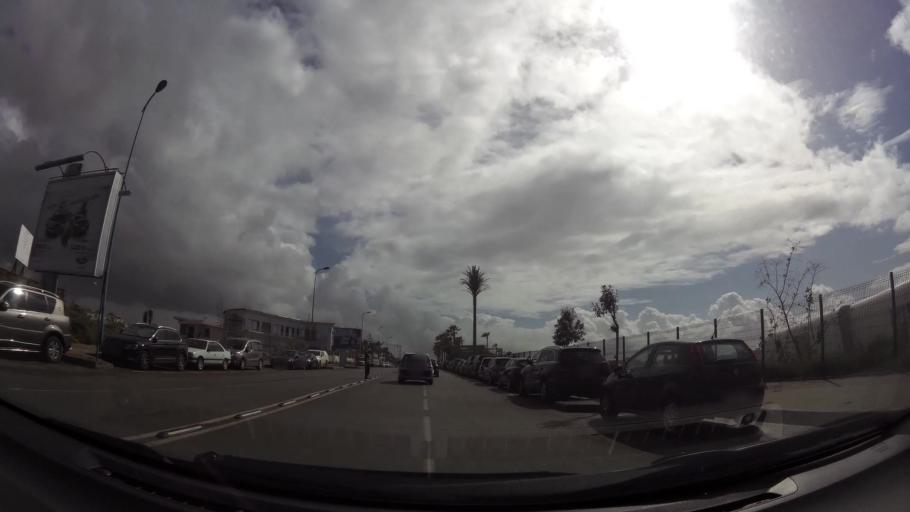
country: MA
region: Grand Casablanca
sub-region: Casablanca
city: Casablanca
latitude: 33.5749
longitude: -7.7061
